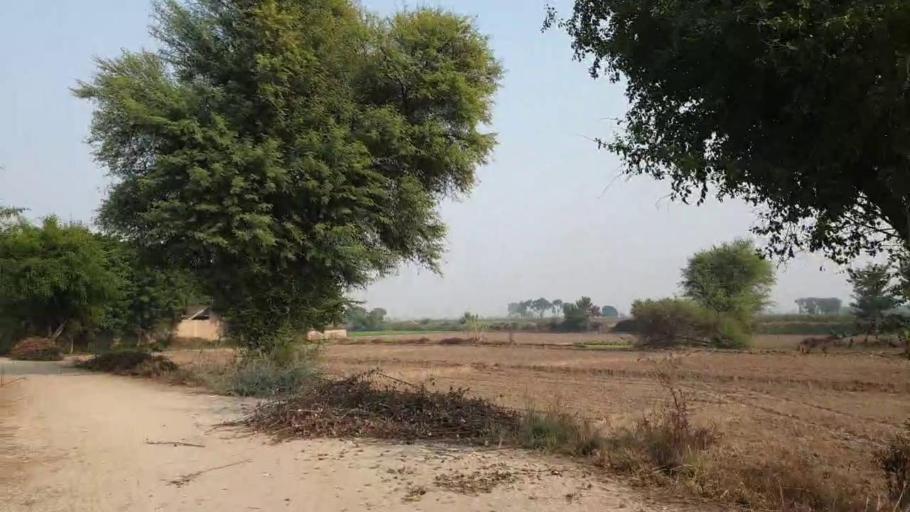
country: PK
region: Sindh
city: Bhan
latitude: 26.5825
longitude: 67.7322
